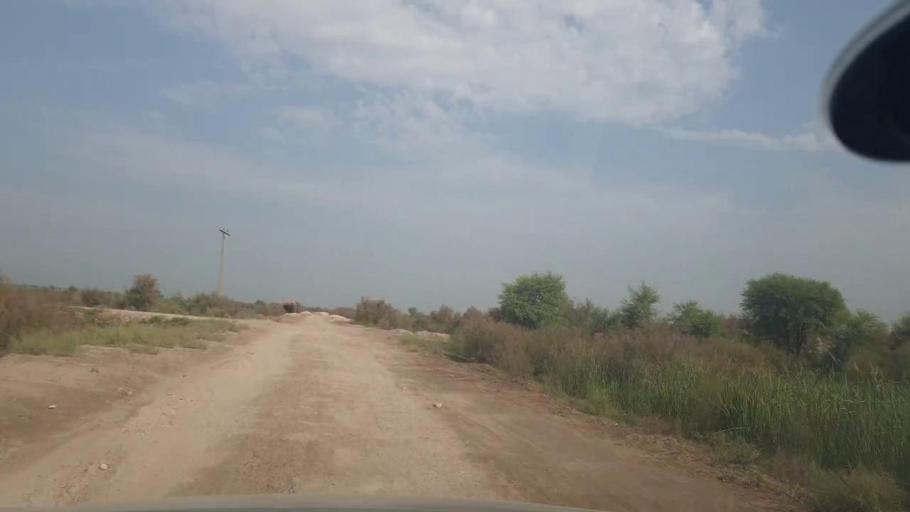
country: PK
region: Balochistan
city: Mehrabpur
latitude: 28.0891
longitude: 68.0969
